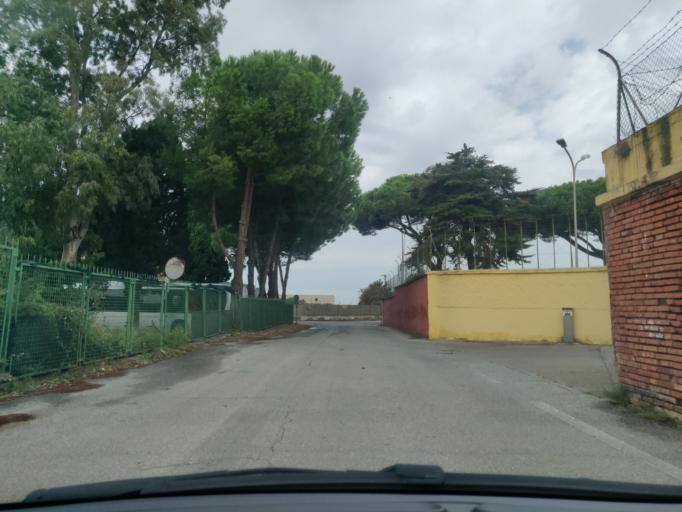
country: IT
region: Latium
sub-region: Citta metropolitana di Roma Capitale
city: Aurelia
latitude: 42.1402
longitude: 11.7860
